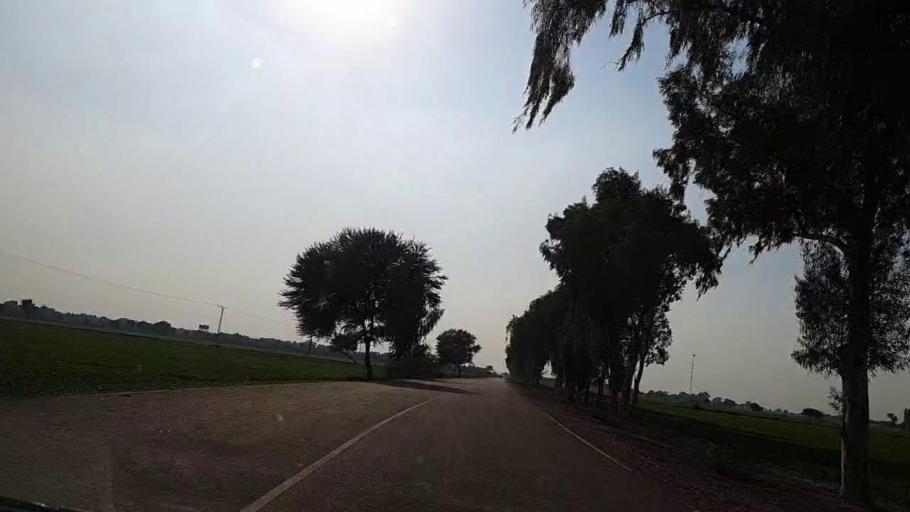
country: PK
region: Sindh
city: Sakrand
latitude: 26.1144
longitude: 68.2458
